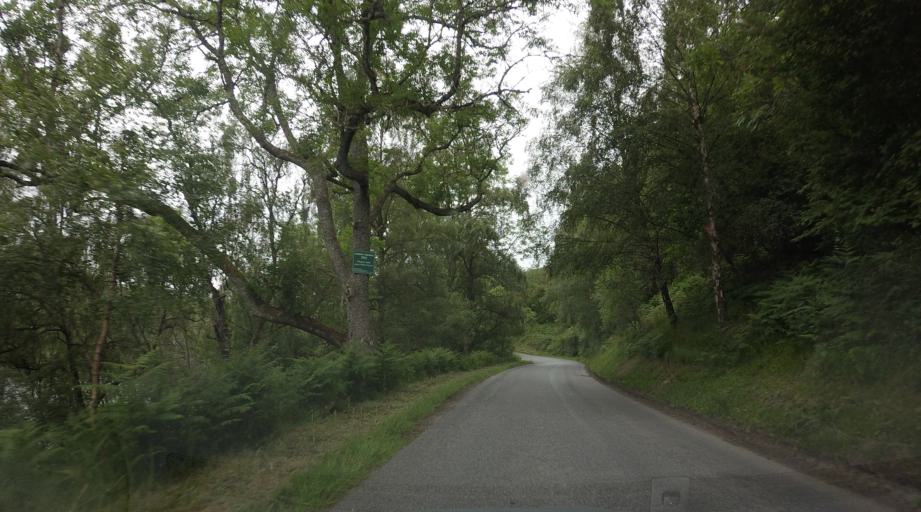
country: GB
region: Scotland
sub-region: Perth and Kinross
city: Pitlochry
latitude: 56.7201
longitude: -3.8325
